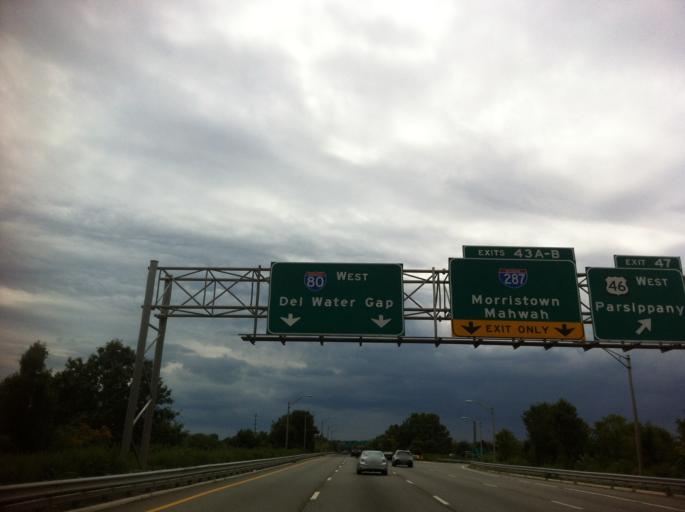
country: US
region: New Jersey
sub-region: Essex County
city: Fairfield
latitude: 40.8696
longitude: -74.3306
